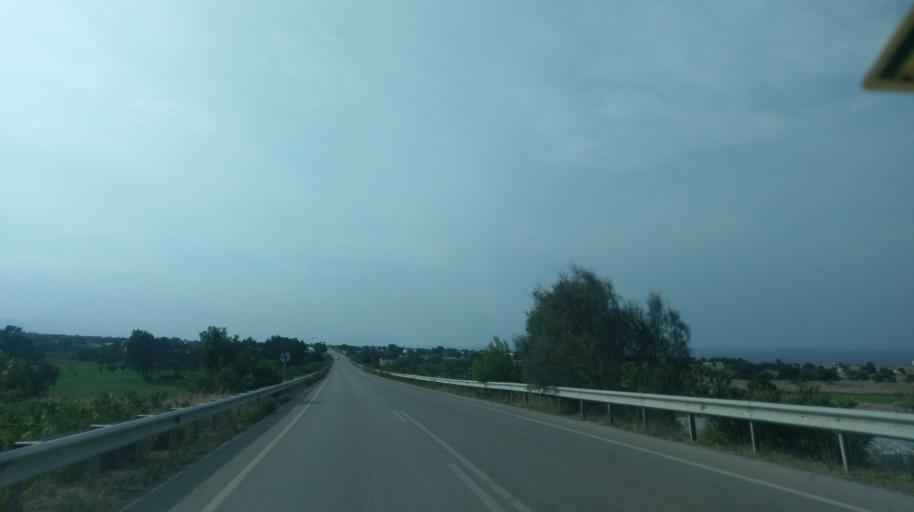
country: CY
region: Ammochostos
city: Lefkonoiko
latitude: 35.4072
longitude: 33.7815
